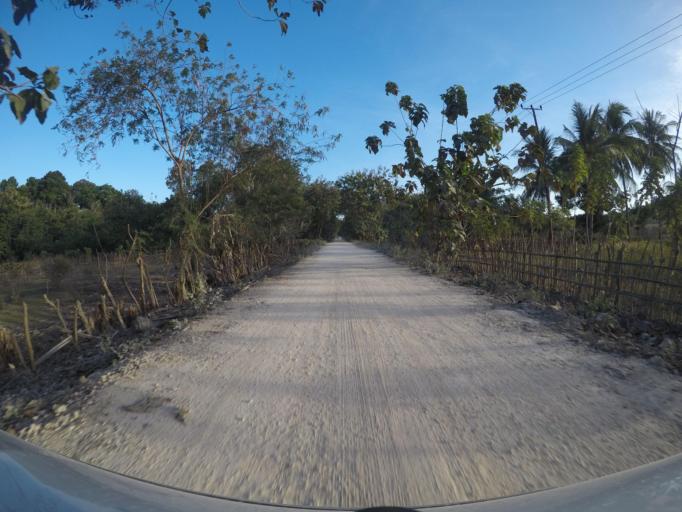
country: TL
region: Viqueque
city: Viqueque
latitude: -8.8808
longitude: 126.5074
